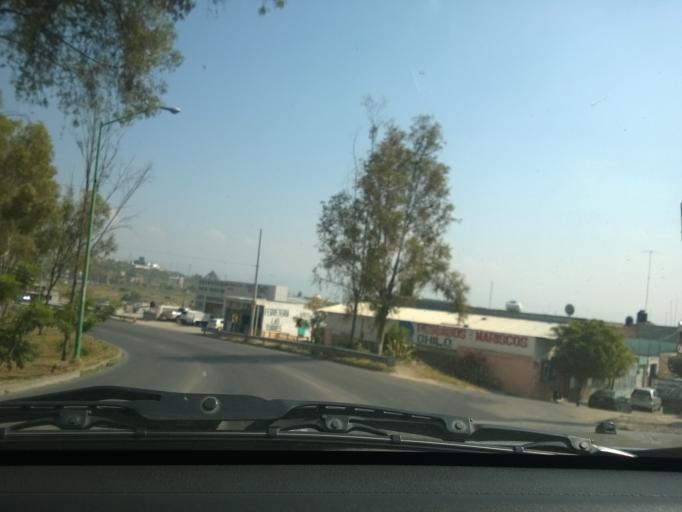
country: MX
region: Guanajuato
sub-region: Leon
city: La Ermita
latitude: 21.1381
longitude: -101.7167
